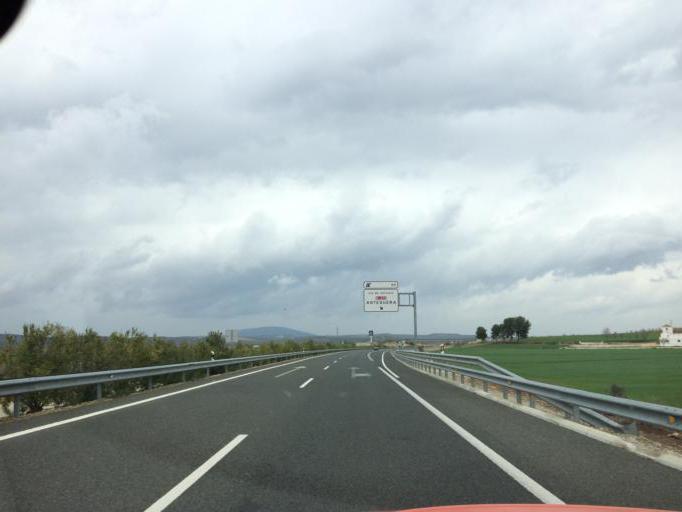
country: ES
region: Andalusia
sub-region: Provincia de Malaga
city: Antequera
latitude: 37.1067
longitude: -4.5599
